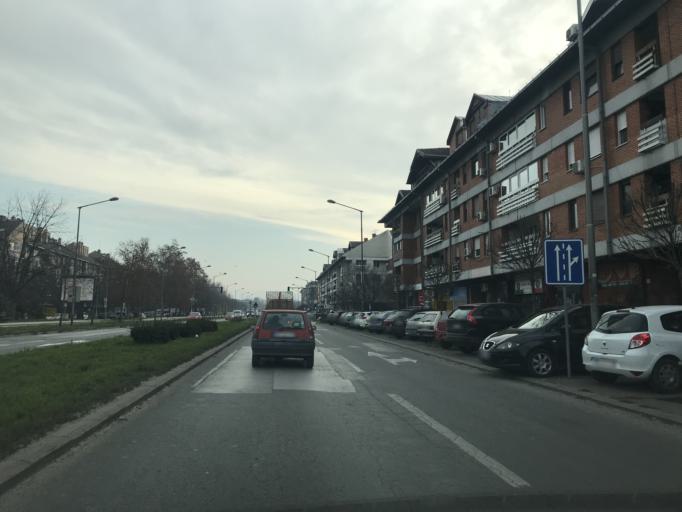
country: RS
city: Veternik
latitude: 45.2530
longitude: 19.7896
